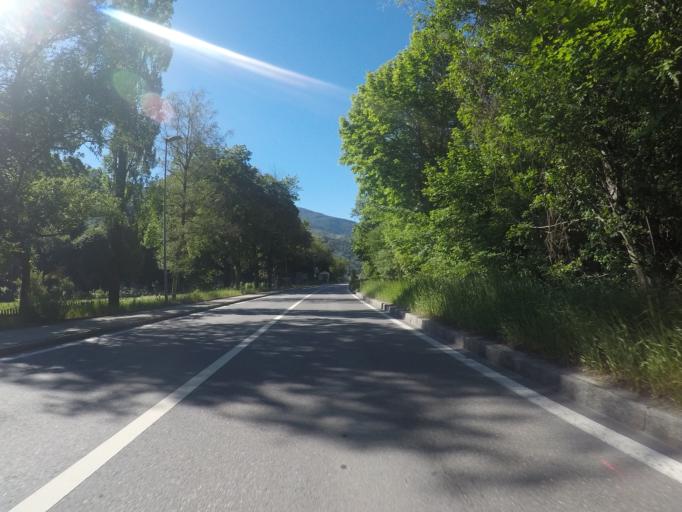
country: CH
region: Valais
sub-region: Visp District
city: Visp
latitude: 46.2884
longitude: 7.8802
